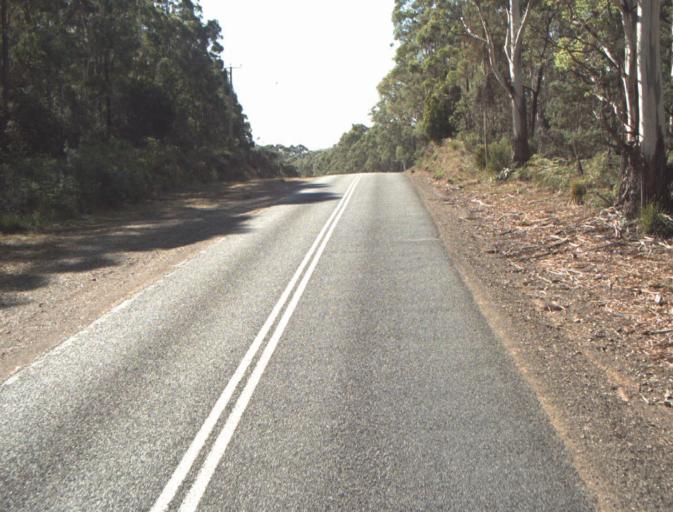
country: AU
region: Tasmania
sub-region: Launceston
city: Mayfield
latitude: -41.3018
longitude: 147.1334
